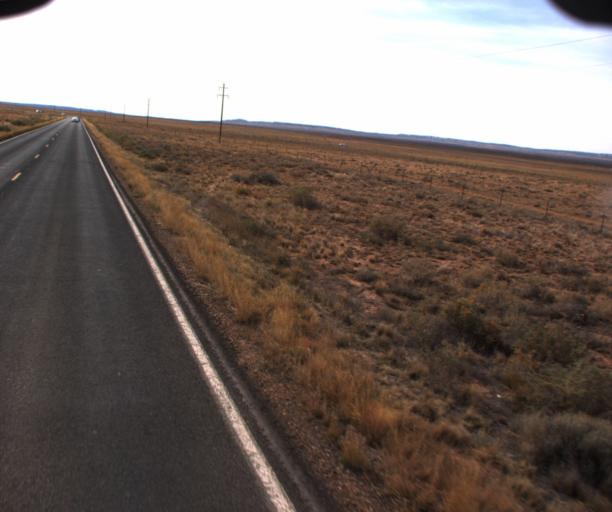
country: US
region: Arizona
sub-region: Apache County
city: Ganado
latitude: 35.9064
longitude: -109.6115
